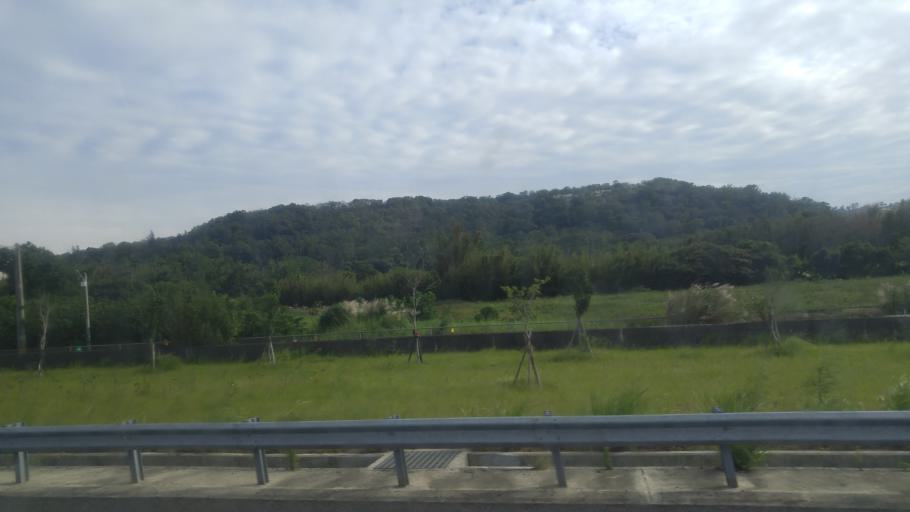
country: TW
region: Taiwan
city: Daxi
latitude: 24.8986
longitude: 121.1449
